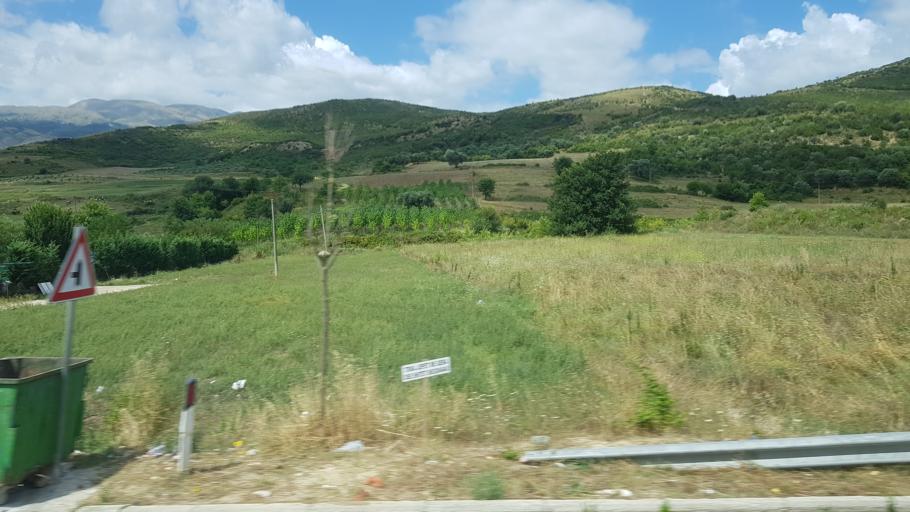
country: AL
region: Gjirokaster
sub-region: Rrethi i Tepelenes
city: Krahes
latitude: 40.4074
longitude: 19.8603
